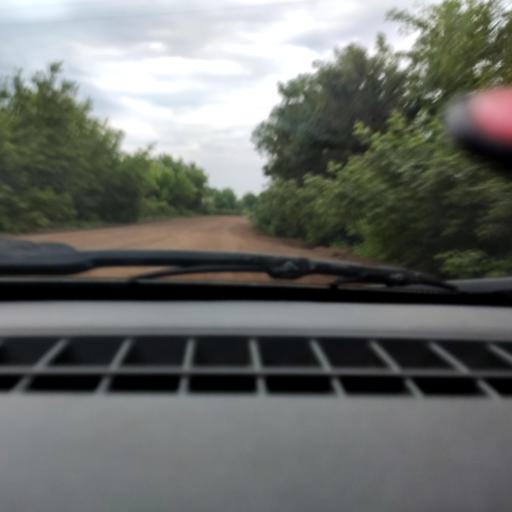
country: RU
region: Bashkortostan
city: Blagoveshchensk
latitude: 54.9260
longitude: 55.9700
